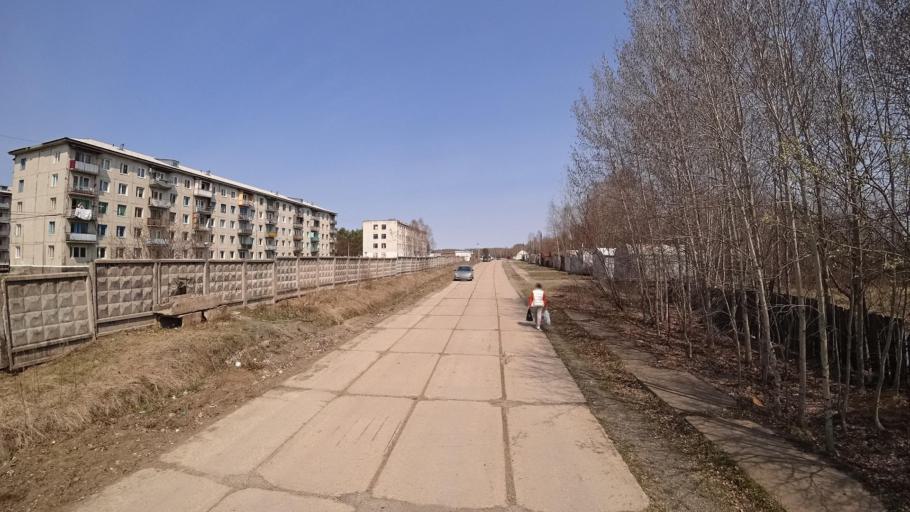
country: RU
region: Khabarovsk Krai
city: Selikhino
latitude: 50.3884
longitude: 137.3736
